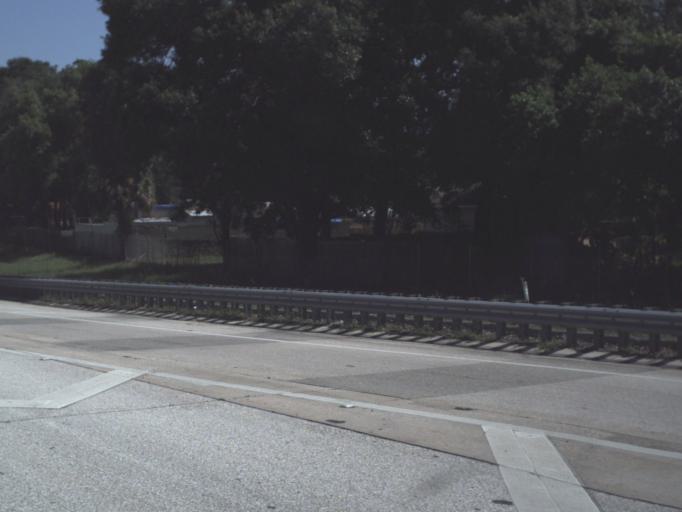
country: US
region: Florida
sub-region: Hillsborough County
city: Egypt Lake-Leto
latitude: 28.0127
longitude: -82.4544
